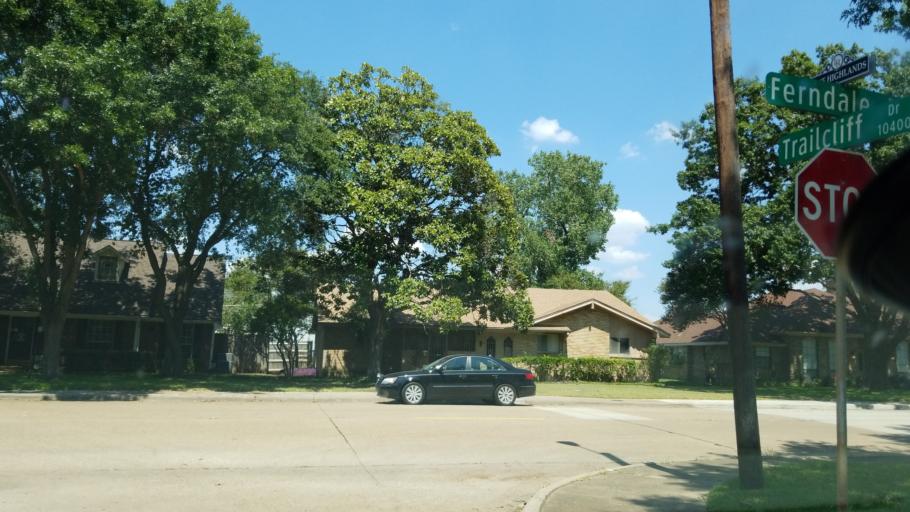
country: US
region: Texas
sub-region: Dallas County
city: Richardson
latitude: 32.8923
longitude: -96.7131
